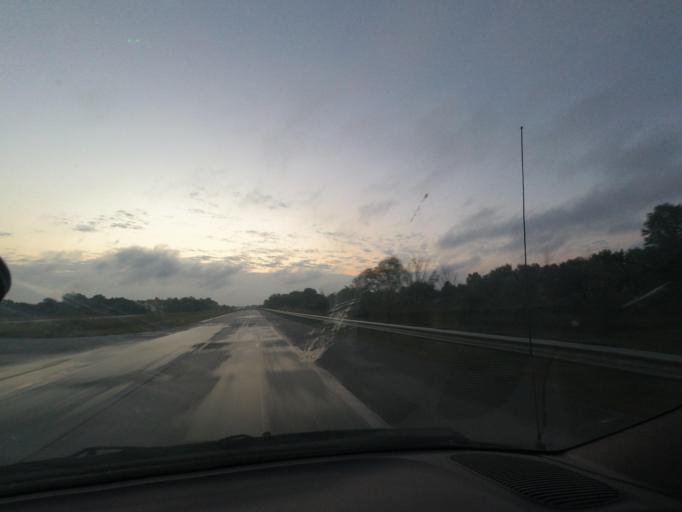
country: US
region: Missouri
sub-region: Linn County
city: Marceline
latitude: 39.7614
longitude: -92.9797
